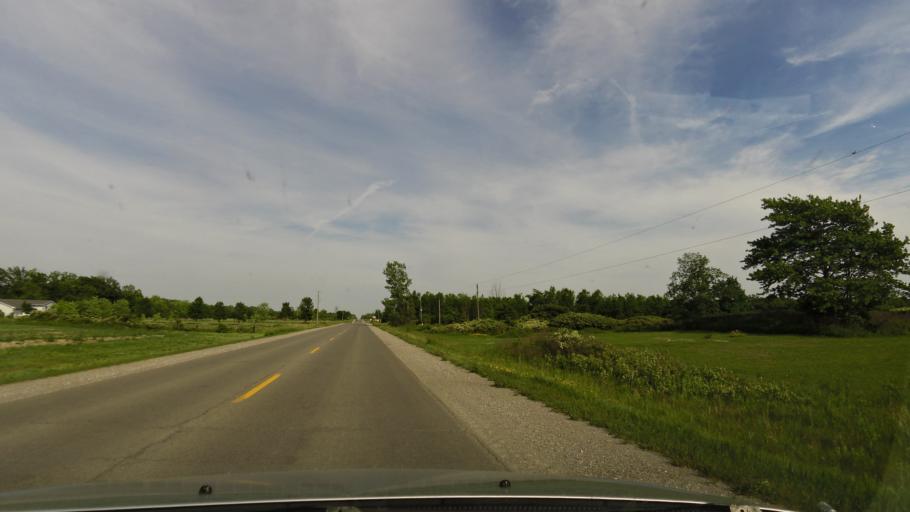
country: CA
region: Ontario
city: Ancaster
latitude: 43.0465
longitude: -80.0581
